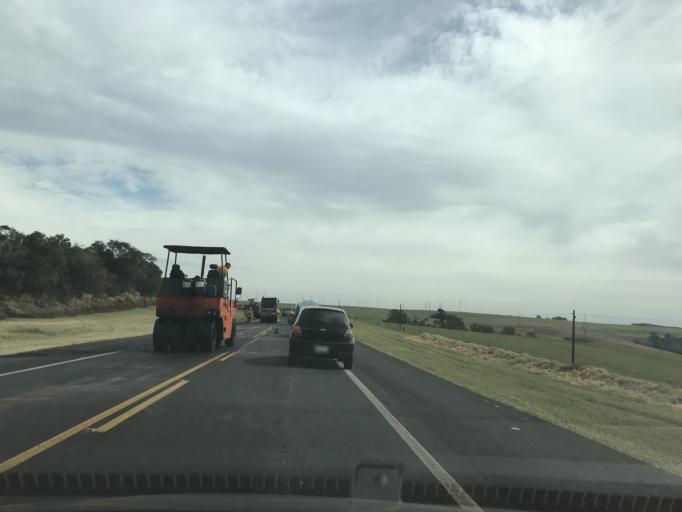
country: BR
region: Parana
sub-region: Cascavel
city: Cascavel
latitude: -25.0740
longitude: -53.6856
